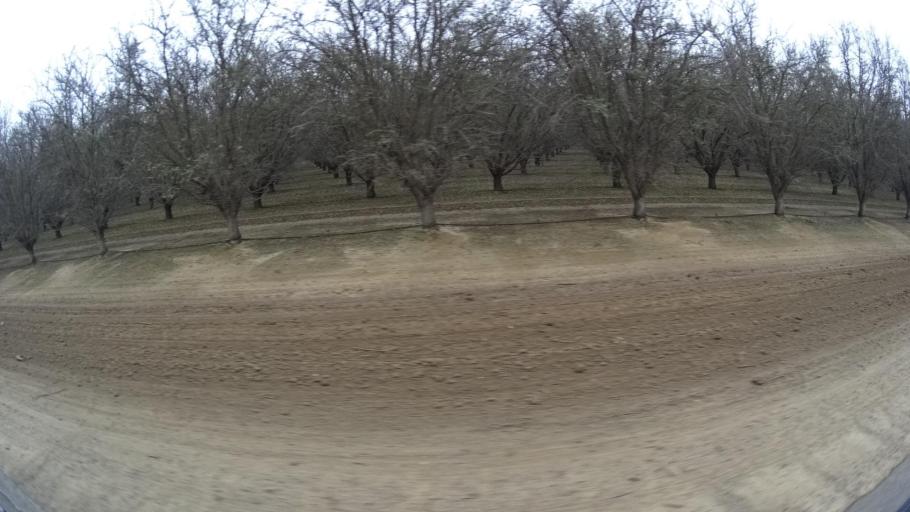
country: US
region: California
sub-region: Kern County
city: Wasco
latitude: 35.5808
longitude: -119.5094
